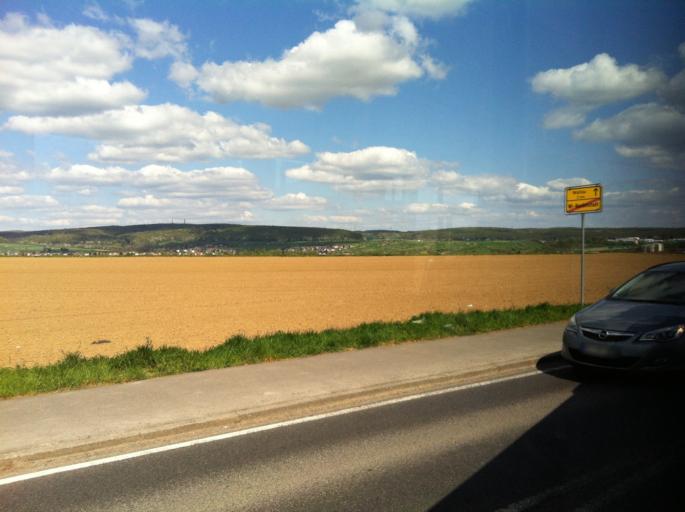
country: DE
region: Hesse
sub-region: Regierungsbezirk Darmstadt
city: Hochheim am Main
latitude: 50.0639
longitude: 8.3526
